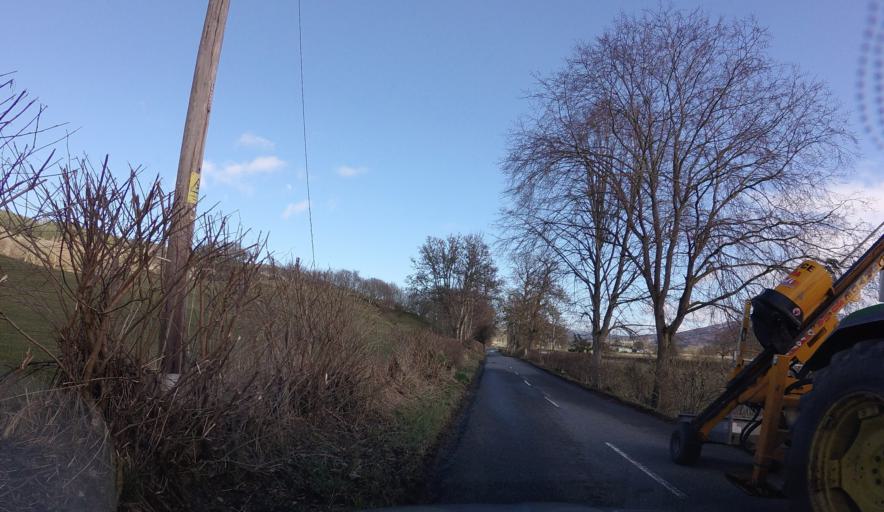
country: GB
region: Scotland
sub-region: Perth and Kinross
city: Pitlochry
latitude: 56.6609
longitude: -3.7547
